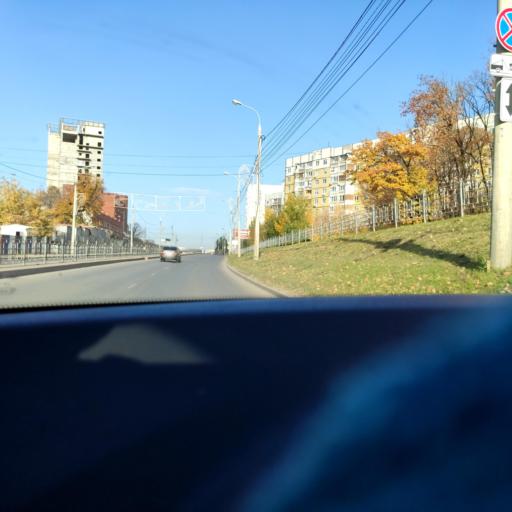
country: RU
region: Samara
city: Samara
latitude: 53.2573
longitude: 50.2042
